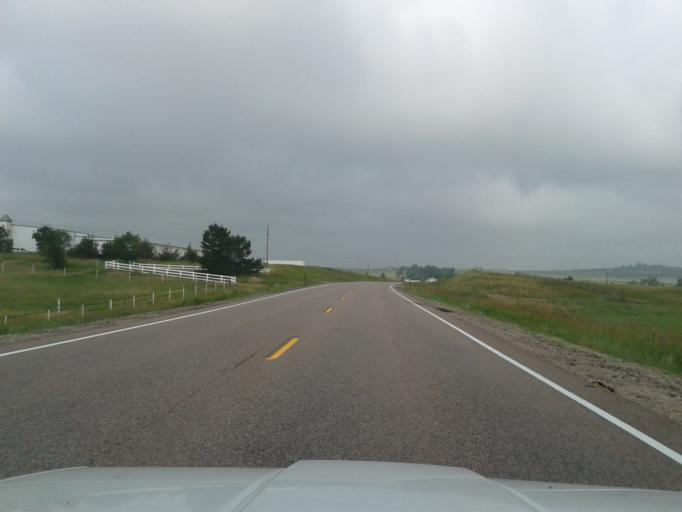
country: US
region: Colorado
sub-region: Elbert County
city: Elizabeth
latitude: 39.2624
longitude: -104.7104
